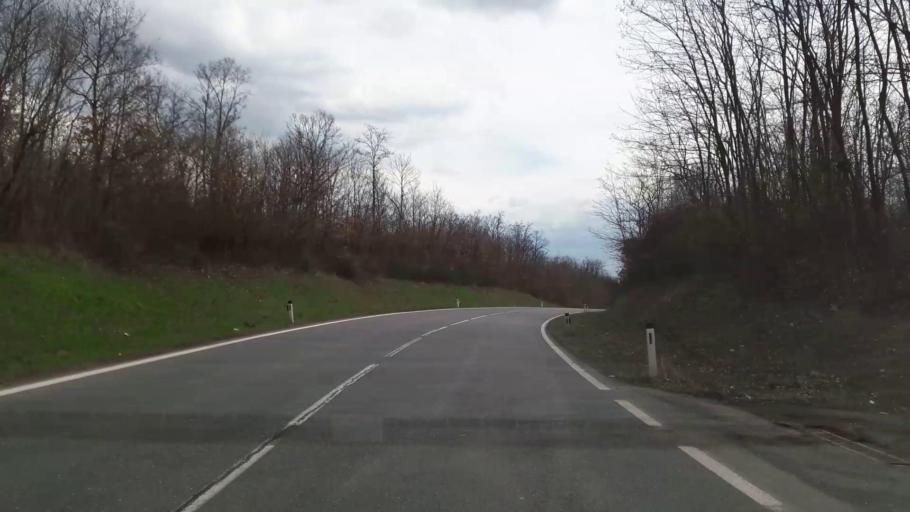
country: AT
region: Lower Austria
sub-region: Politischer Bezirk Mistelbach
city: Mistelbach
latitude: 48.5298
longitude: 16.6014
